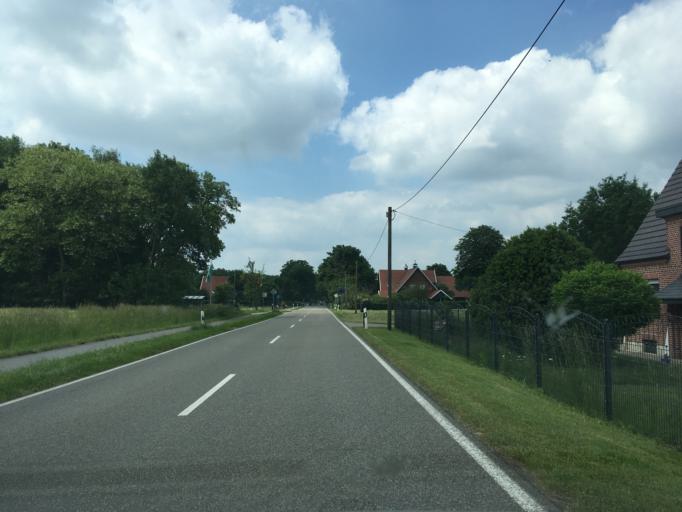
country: DE
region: North Rhine-Westphalia
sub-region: Regierungsbezirk Munster
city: Rhede
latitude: 51.7916
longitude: 6.7638
